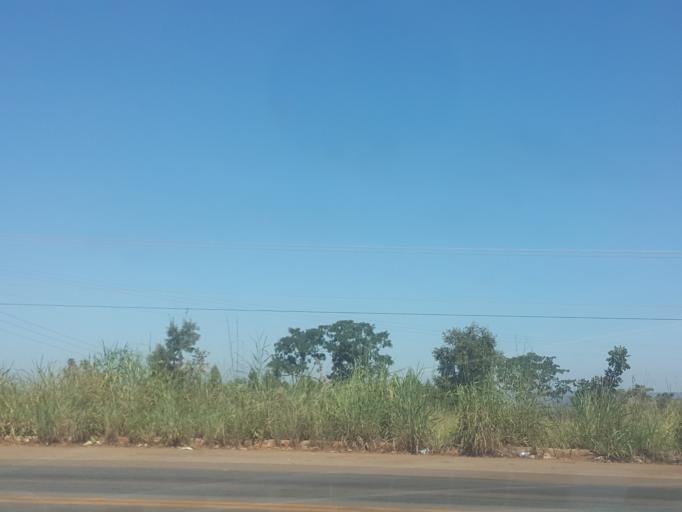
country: BR
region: Goias
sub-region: Luziania
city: Luziania
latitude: -16.0090
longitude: -48.1621
